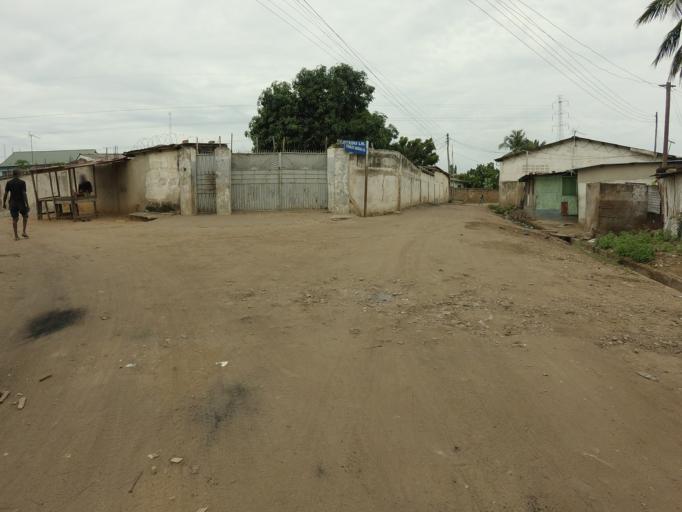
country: GH
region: Greater Accra
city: Accra
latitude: 5.5885
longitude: -0.2163
